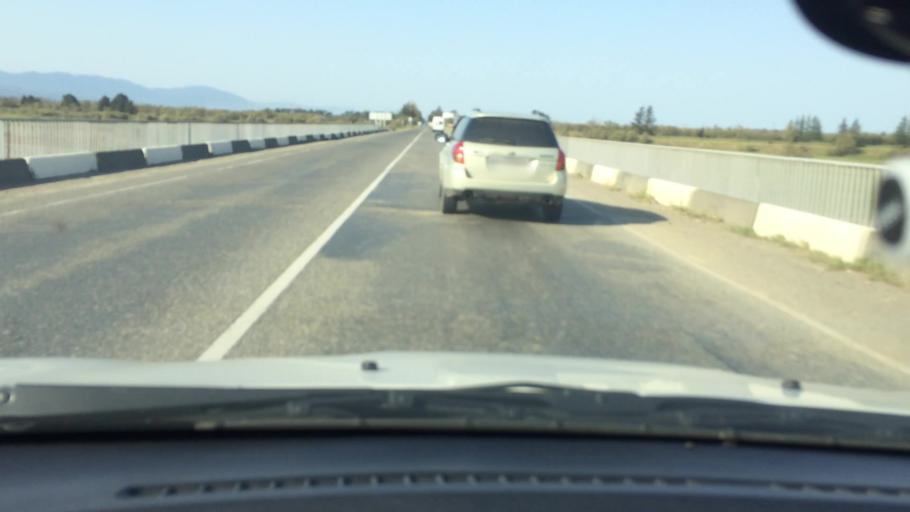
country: GE
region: Imereti
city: K'ulashi
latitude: 42.1737
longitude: 42.4290
